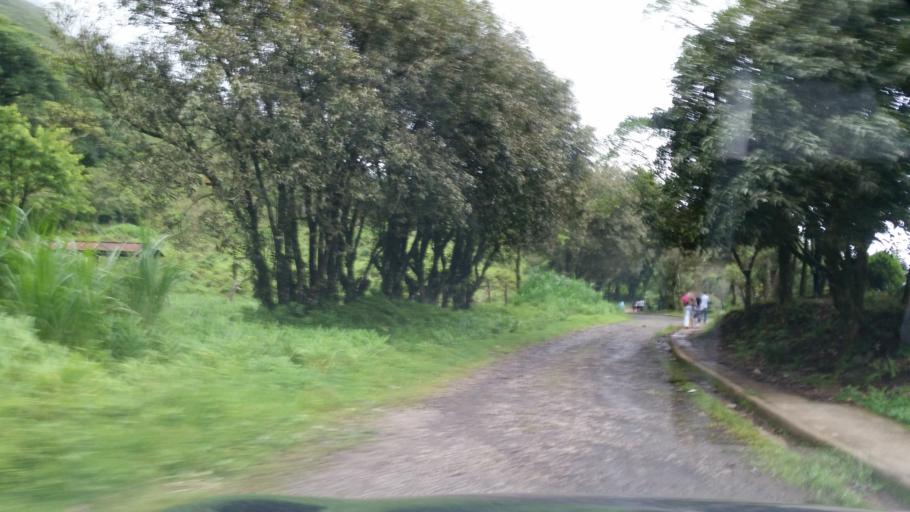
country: NI
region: Jinotega
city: San Jose de Bocay
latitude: 13.2822
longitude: -85.7163
